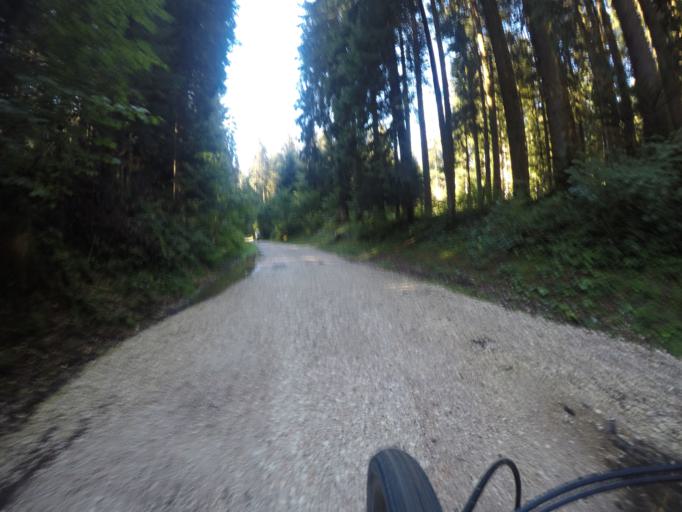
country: IT
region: Veneto
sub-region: Provincia di Vicenza
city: Canove di Roana
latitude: 45.8454
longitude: 11.4679
